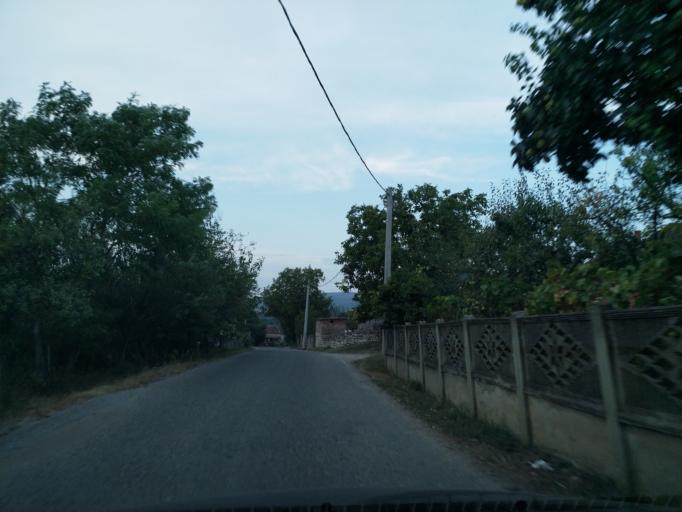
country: RS
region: Central Serbia
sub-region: Pomoravski Okrug
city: Paracin
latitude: 43.8498
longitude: 21.5279
